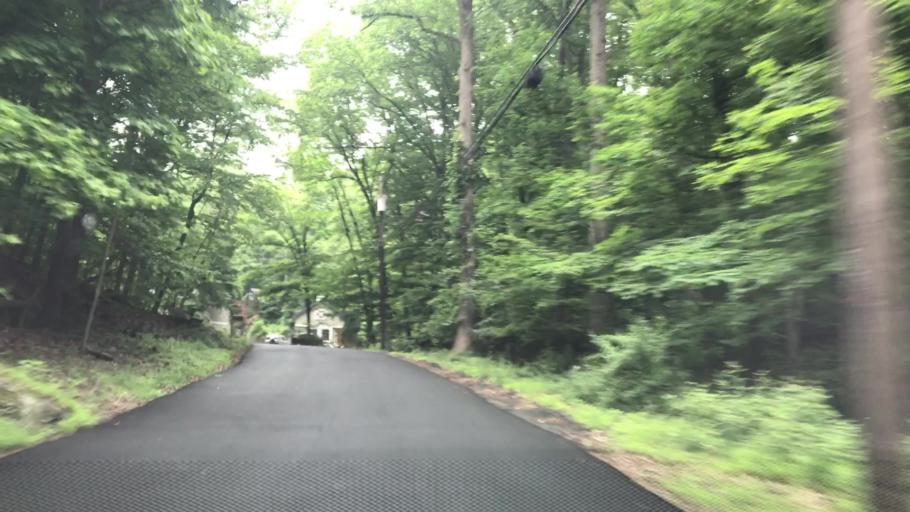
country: US
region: New Jersey
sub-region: Hunterdon County
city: Lebanon
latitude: 40.6674
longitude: -74.8331
